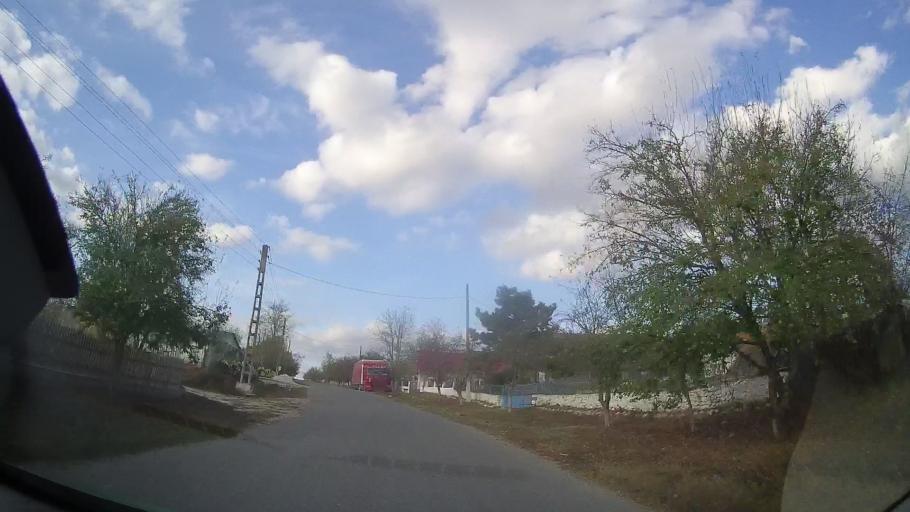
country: RO
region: Constanta
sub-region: Comuna Cerchezu
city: Cerchezu
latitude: 43.8606
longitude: 28.1014
